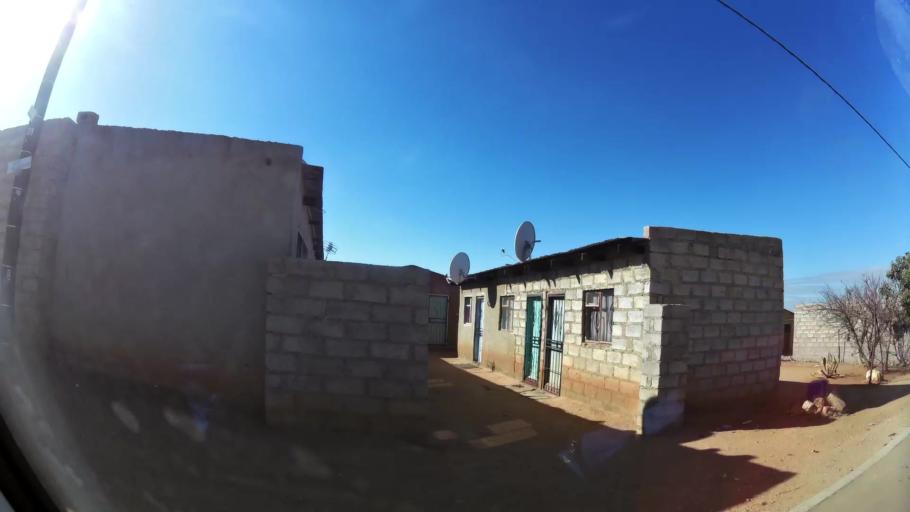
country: ZA
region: Gauteng
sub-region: City of Johannesburg Metropolitan Municipality
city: Diepsloot
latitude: -25.9066
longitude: 28.0935
